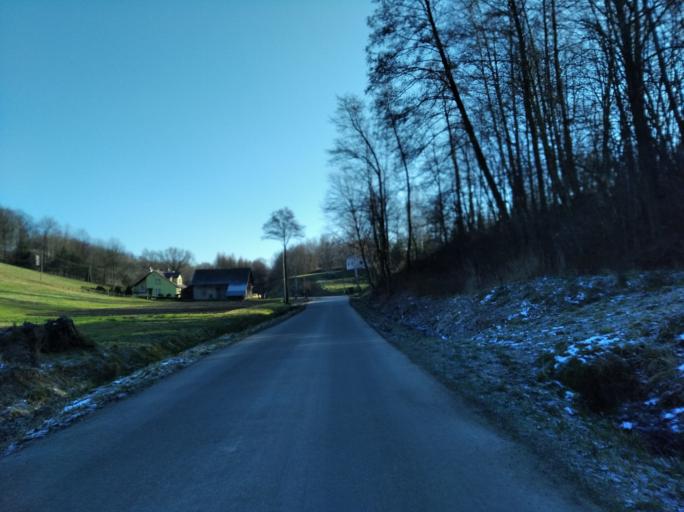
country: PL
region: Subcarpathian Voivodeship
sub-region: Powiat strzyzowski
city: Wysoka Strzyzowska
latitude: 49.8456
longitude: 21.7645
